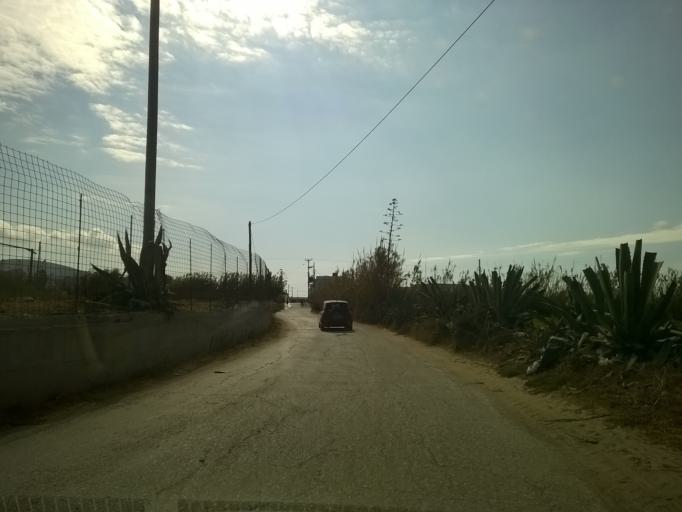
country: GR
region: South Aegean
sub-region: Nomos Kykladon
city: Naxos
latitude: 37.0742
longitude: 25.3852
